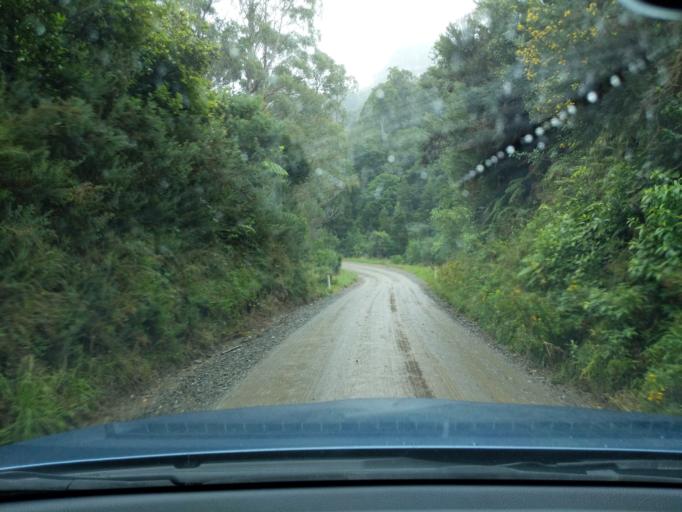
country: NZ
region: Tasman
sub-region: Tasman District
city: Takaka
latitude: -40.6459
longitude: 172.4737
